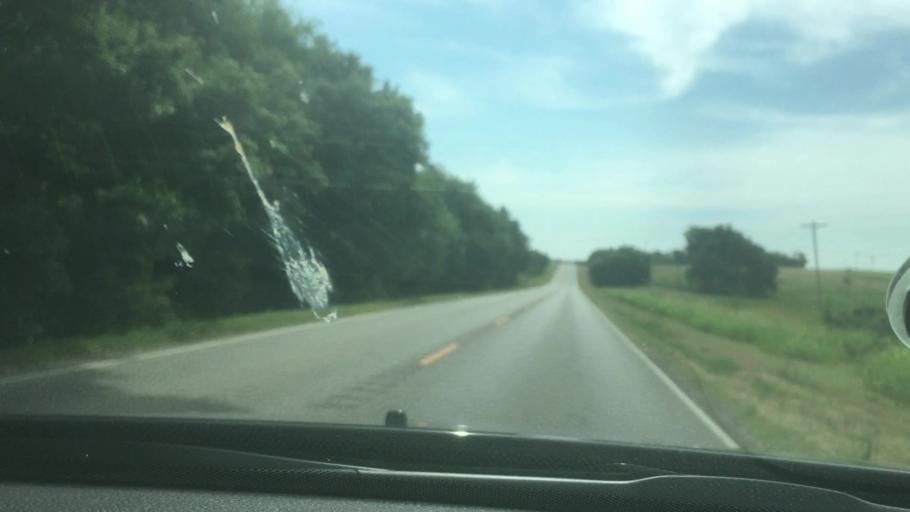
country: US
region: Oklahoma
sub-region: Garvin County
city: Maysville
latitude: 34.8138
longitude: -97.3875
